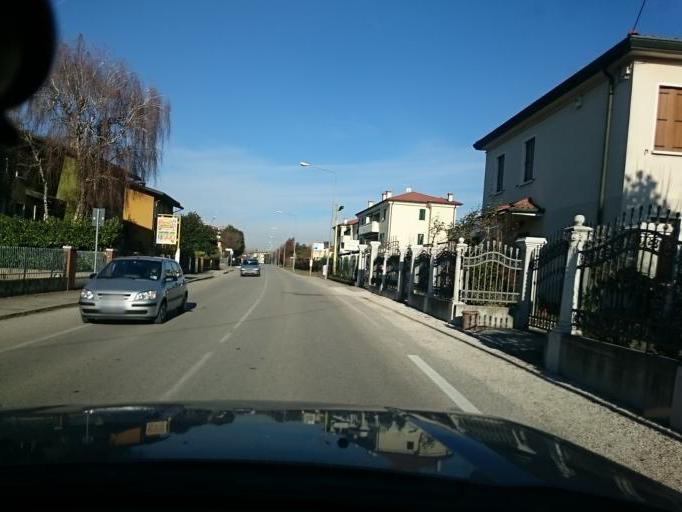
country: IT
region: Veneto
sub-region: Provincia di Venezia
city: Dolo
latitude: 45.4159
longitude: 12.0821
